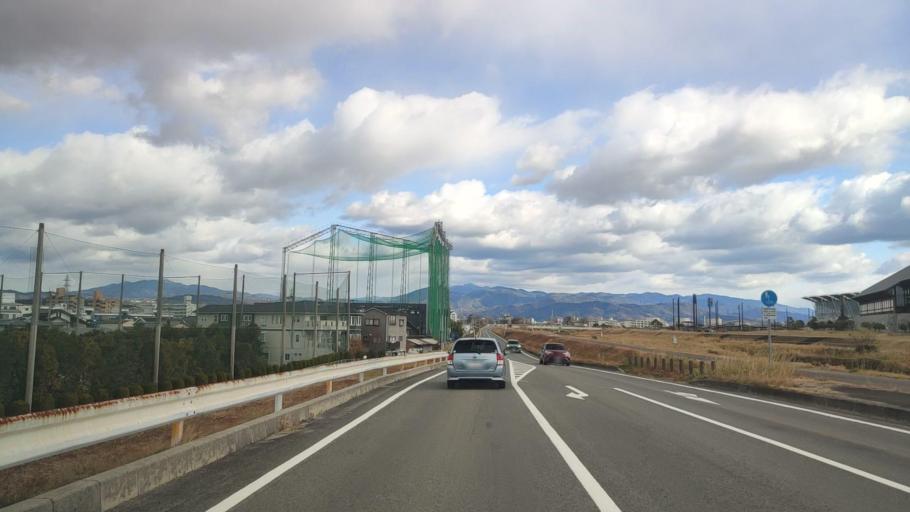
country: JP
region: Ehime
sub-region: Shikoku-chuo Shi
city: Matsuyama
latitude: 33.8112
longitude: 132.7418
